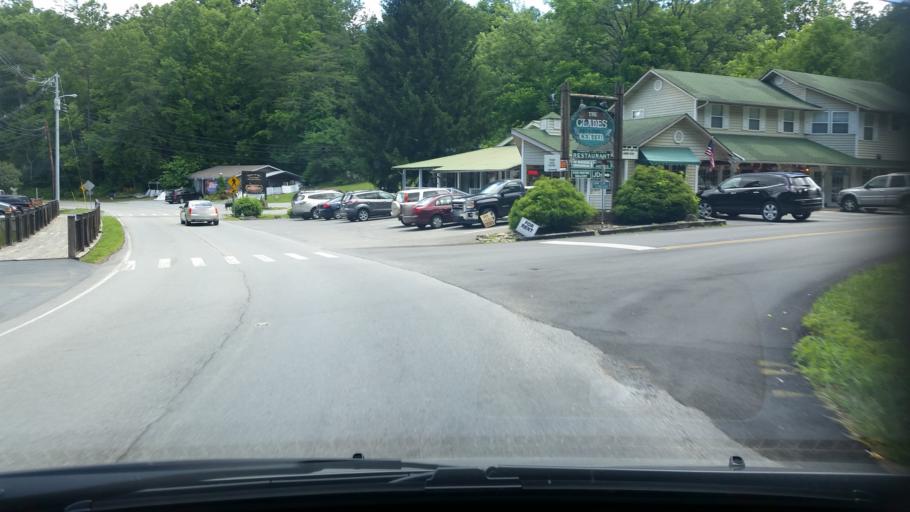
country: US
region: Tennessee
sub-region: Sevier County
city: Gatlinburg
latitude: 35.7399
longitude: -83.4609
